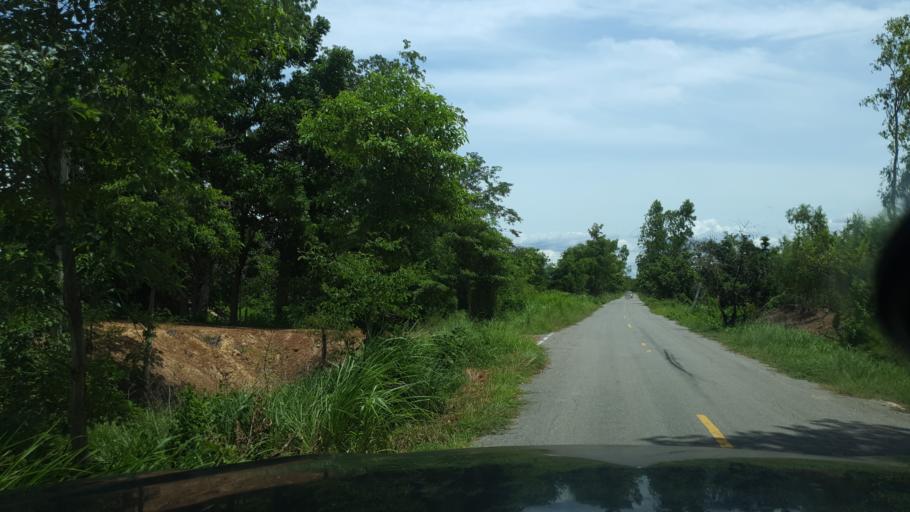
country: TH
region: Sukhothai
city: Ban Na
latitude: 17.1149
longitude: 99.6765
